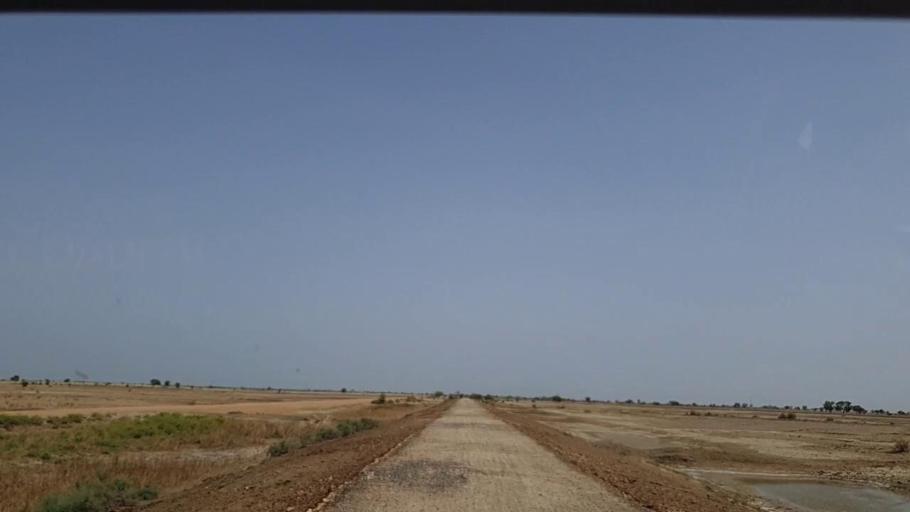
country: PK
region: Sindh
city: Johi
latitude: 26.7754
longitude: 67.6535
